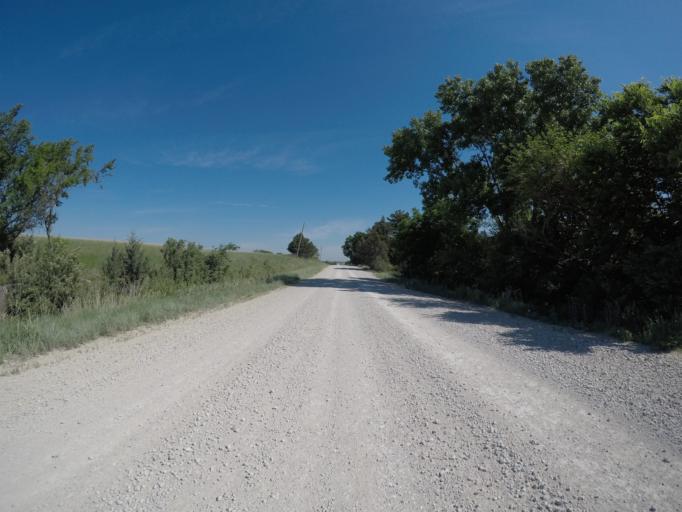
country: US
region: Kansas
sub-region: Wabaunsee County
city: Alma
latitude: 38.9885
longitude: -96.1139
